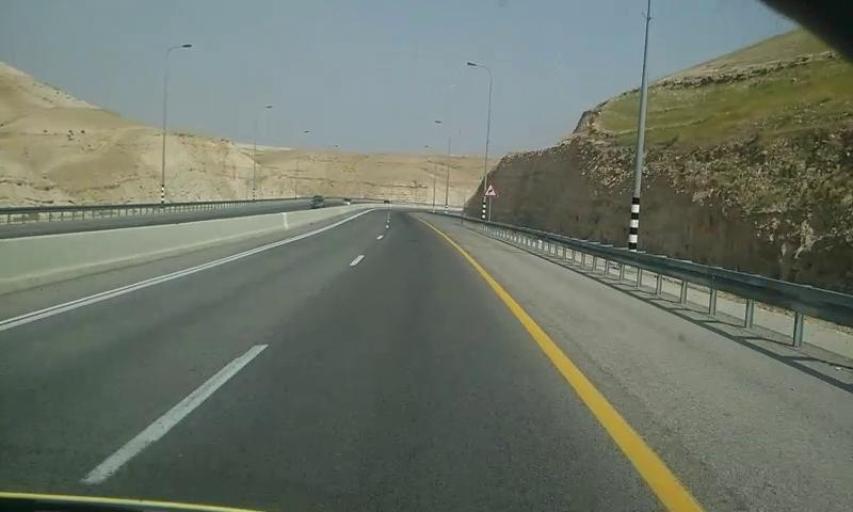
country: PS
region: West Bank
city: Jericho
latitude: 31.7992
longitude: 35.4366
